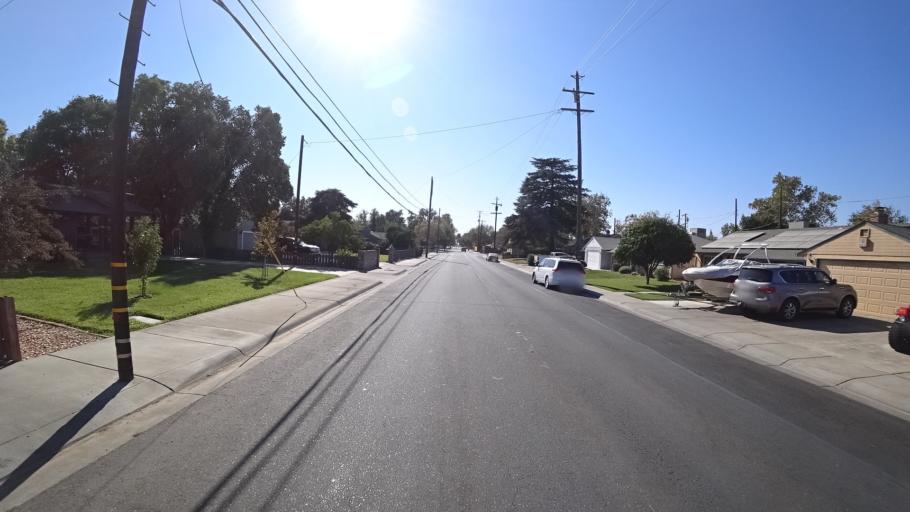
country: US
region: California
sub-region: Yolo County
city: Woodland
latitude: 38.6678
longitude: -121.7841
